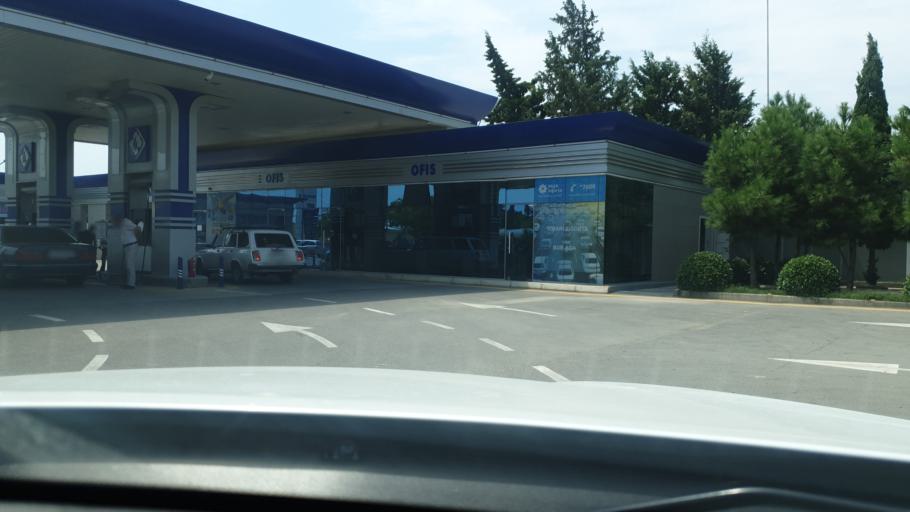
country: AZ
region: Baki
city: Qaracuxur
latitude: 40.3997
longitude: 50.0002
